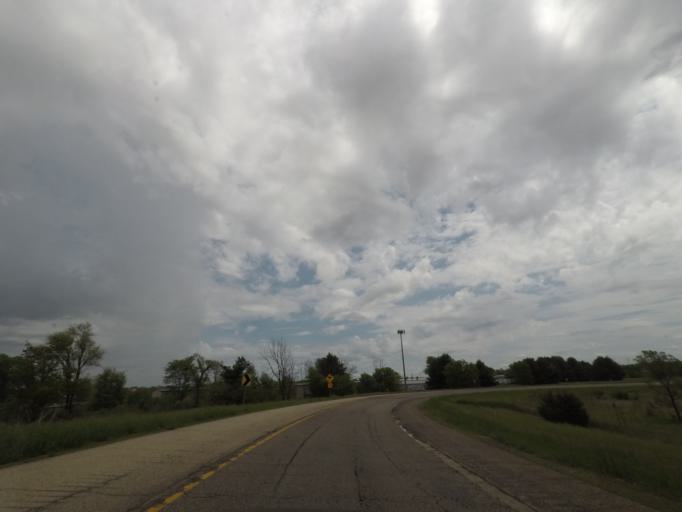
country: US
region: Illinois
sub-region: Winnebago County
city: Cherry Valley
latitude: 42.2225
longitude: -89.0098
